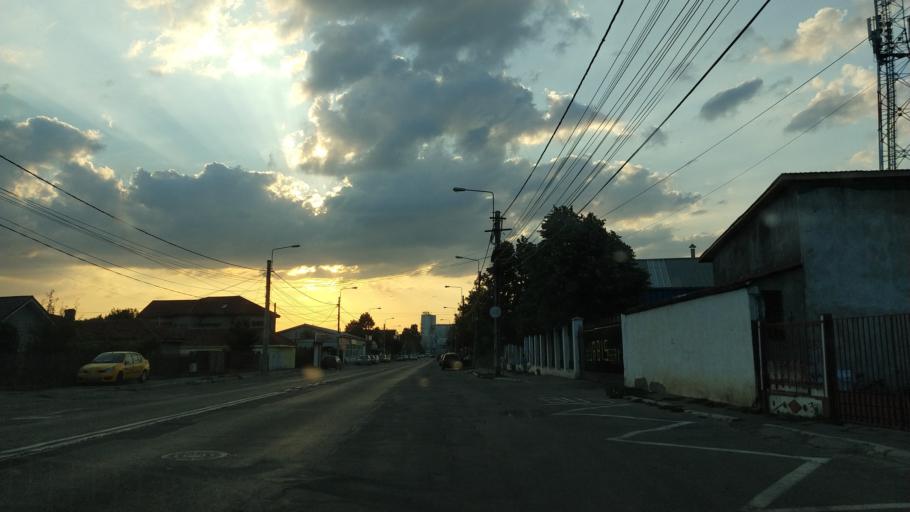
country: RO
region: Buzau
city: Buzau
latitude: 45.1611
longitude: 26.7972
